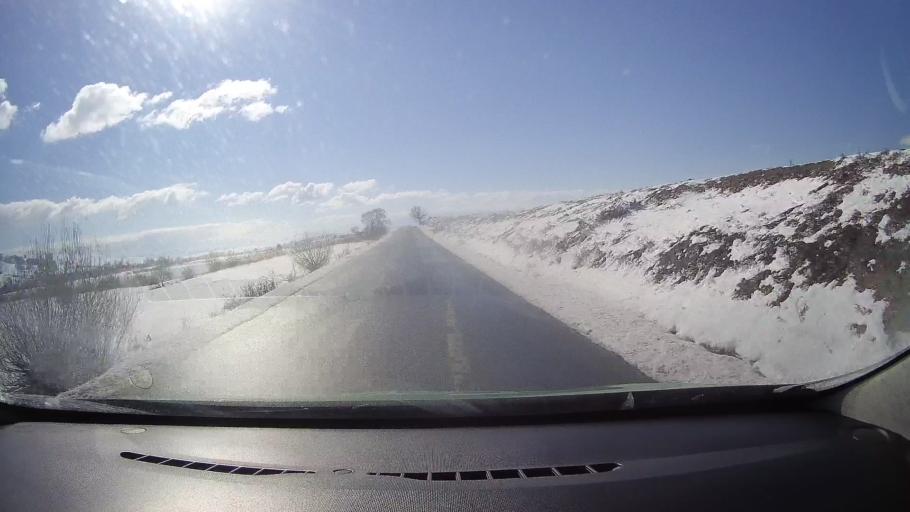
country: RO
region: Sibiu
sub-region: Comuna Rosia
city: Rosia
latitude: 45.8559
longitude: 24.3107
